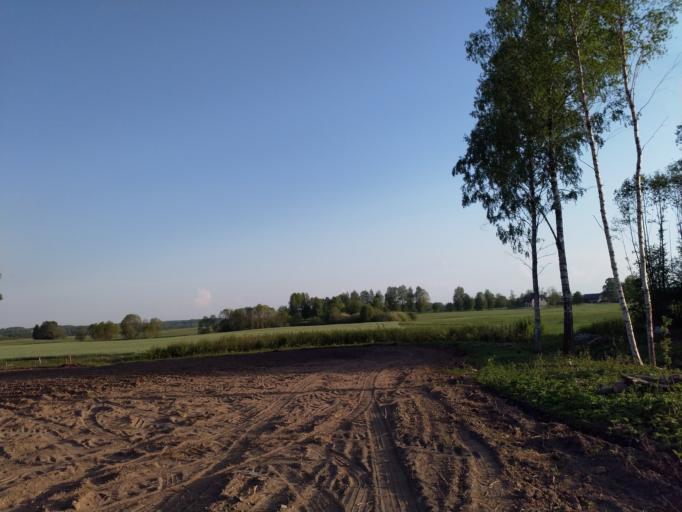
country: LV
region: Aizpute
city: Aizpute
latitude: 56.8297
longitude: 21.7821
